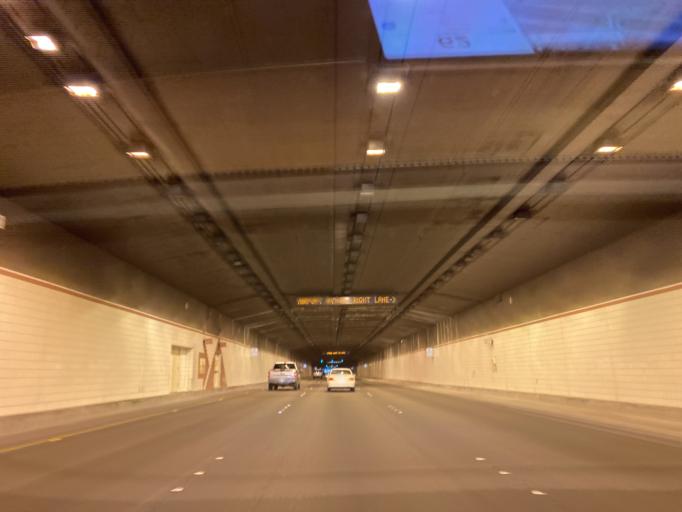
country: US
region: Nevada
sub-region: Clark County
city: Paradise
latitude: 36.0727
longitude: -115.1455
